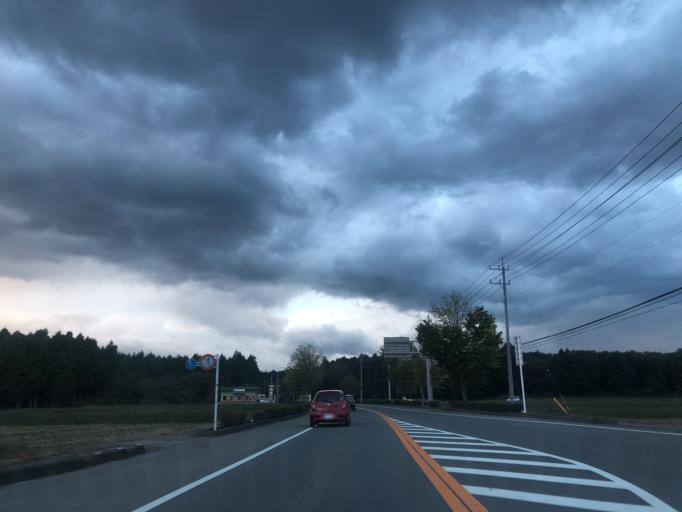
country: JP
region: Tochigi
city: Kuroiso
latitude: 36.9554
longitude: 140.0028
